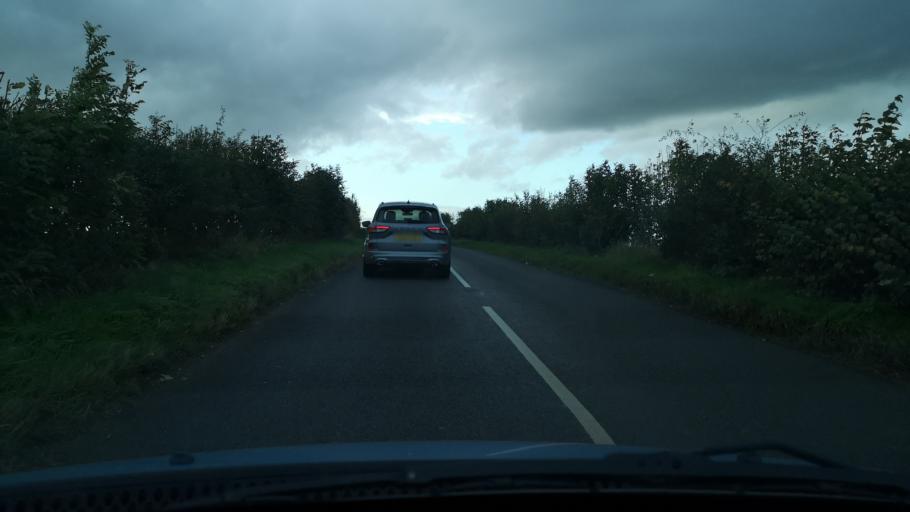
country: GB
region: England
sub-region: Doncaster
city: Norton
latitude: 53.6319
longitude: -1.1926
